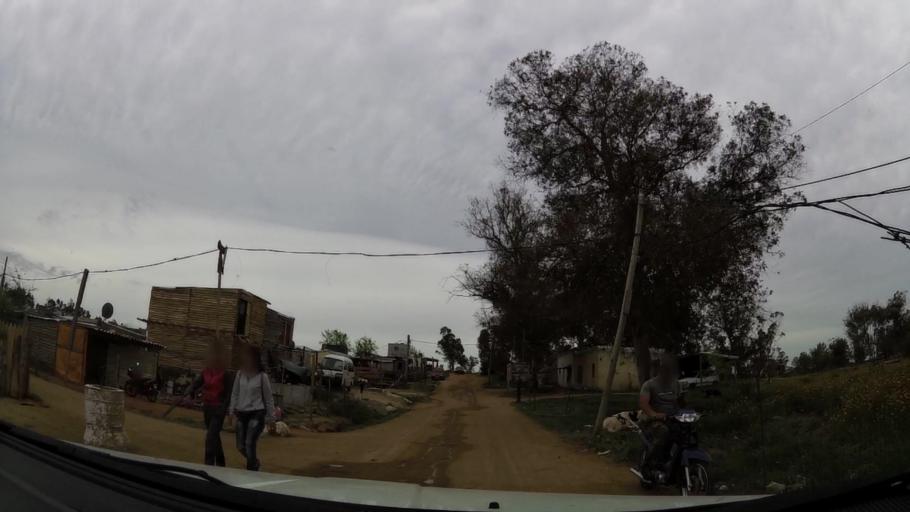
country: UY
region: Maldonado
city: Maldonado
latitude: -34.8890
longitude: -54.9565
